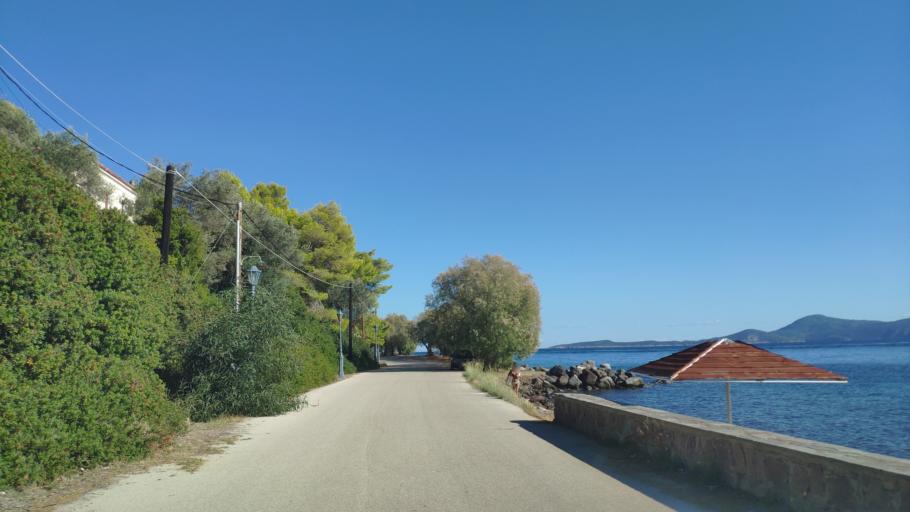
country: GR
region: Attica
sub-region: Nomos Piraios
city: Poros
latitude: 37.5871
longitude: 23.3995
